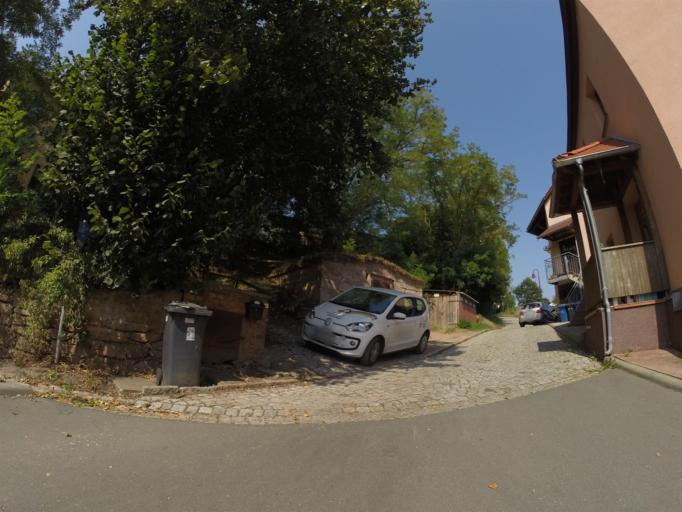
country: DE
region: Thuringia
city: Rausdorf
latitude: 50.8678
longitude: 11.6995
